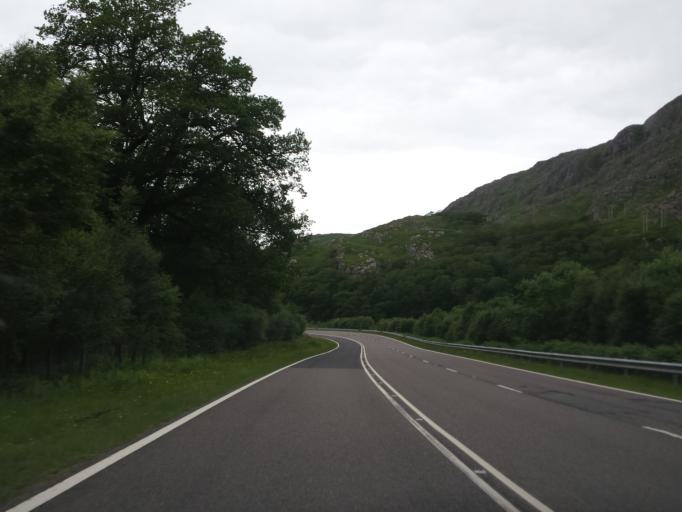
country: GB
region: Scotland
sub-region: Argyll and Bute
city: Isle Of Mull
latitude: 56.8920
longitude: -5.7178
